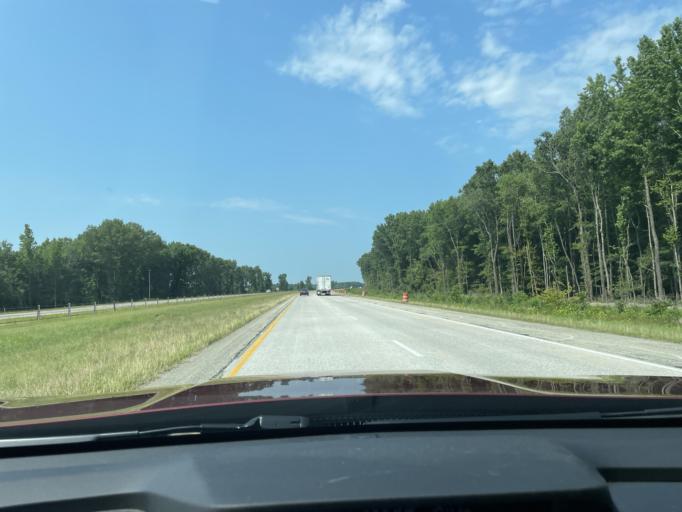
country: US
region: Arkansas
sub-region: White County
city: Searcy
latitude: 35.1540
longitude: -91.7888
